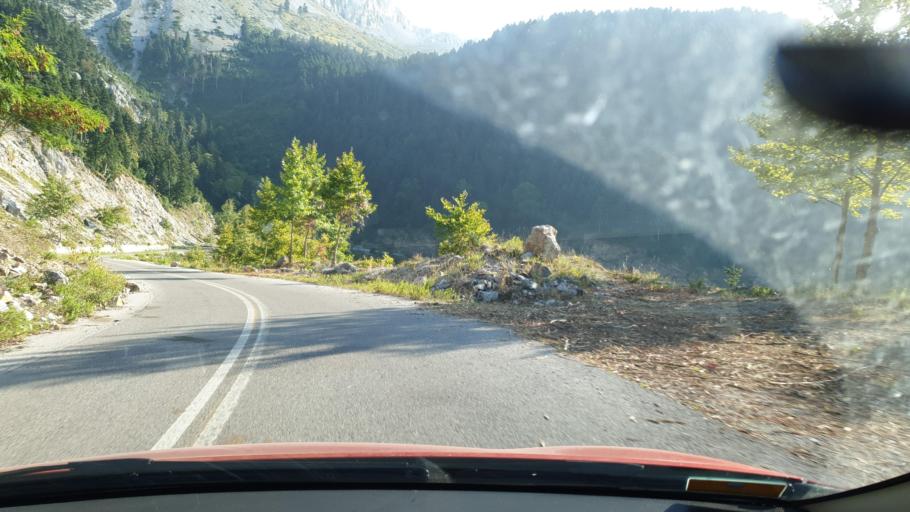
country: GR
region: Central Greece
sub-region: Nomos Evvoias
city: Yimnon
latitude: 38.5969
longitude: 23.9065
